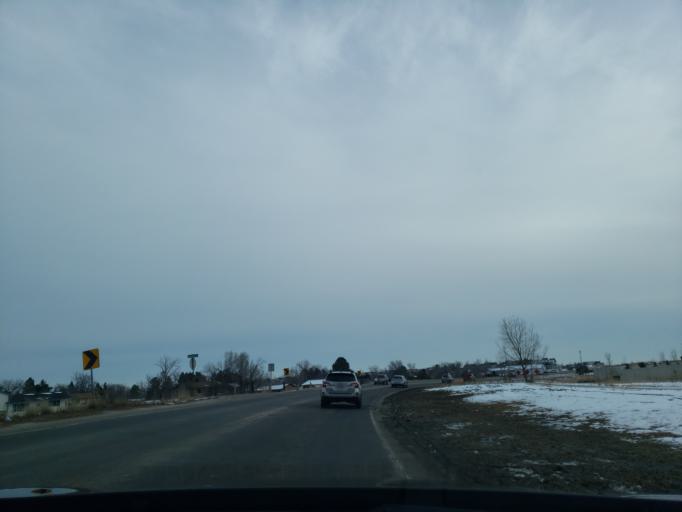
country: US
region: Colorado
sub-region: Larimer County
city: Campion
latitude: 40.3460
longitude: -105.0943
